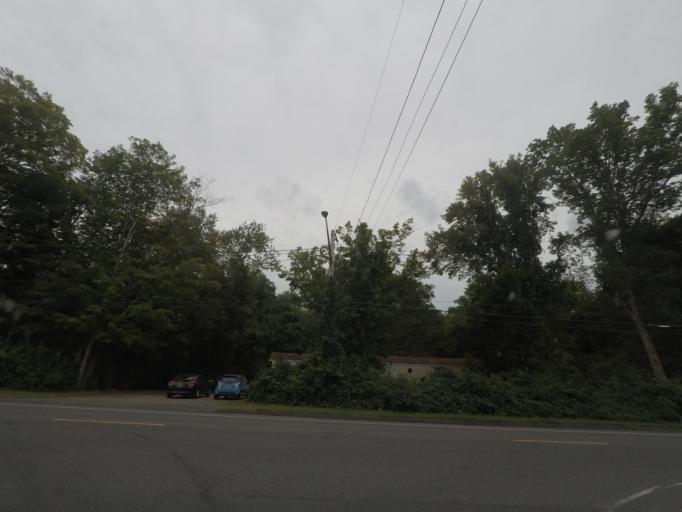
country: US
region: Massachusetts
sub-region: Hampshire County
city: Ware
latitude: 42.2111
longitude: -72.2446
